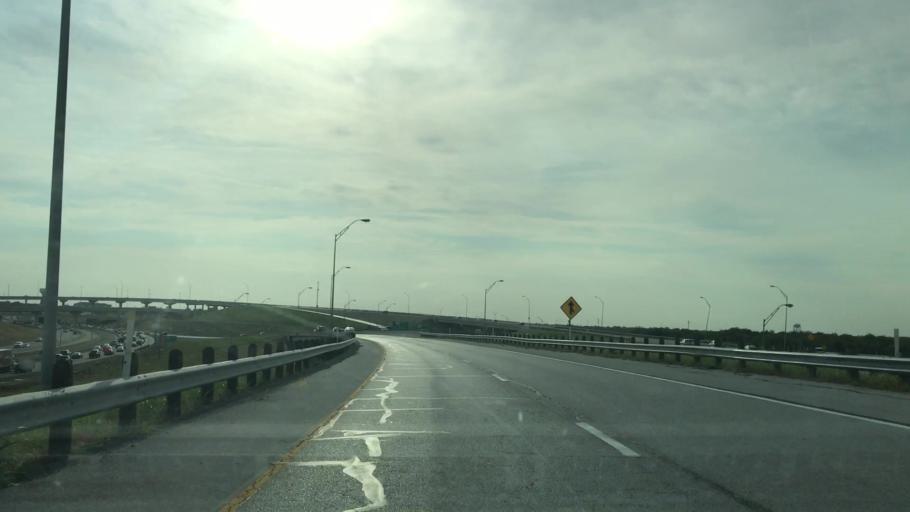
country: US
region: Texas
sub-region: Tarrant County
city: Euless
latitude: 32.8392
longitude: -97.0531
